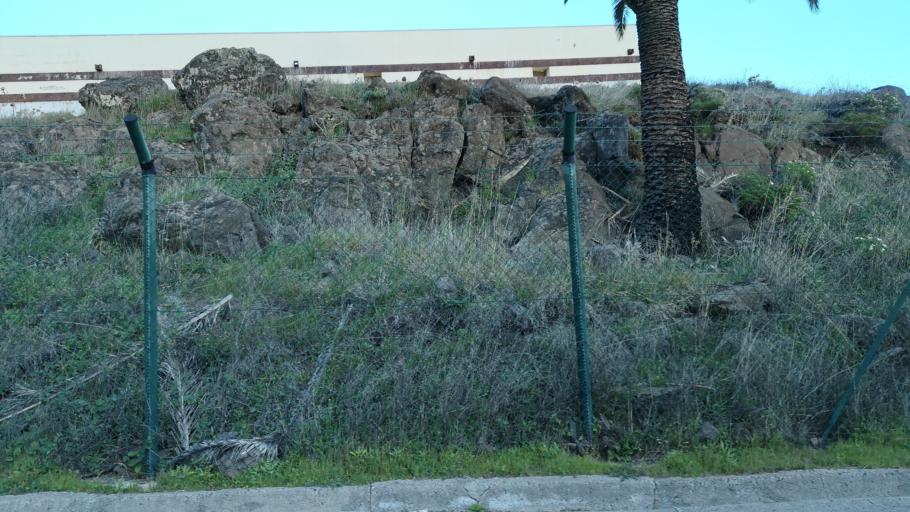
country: ES
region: Canary Islands
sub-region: Provincia de Santa Cruz de Tenerife
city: Alajero
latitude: 28.0764
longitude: -17.2423
